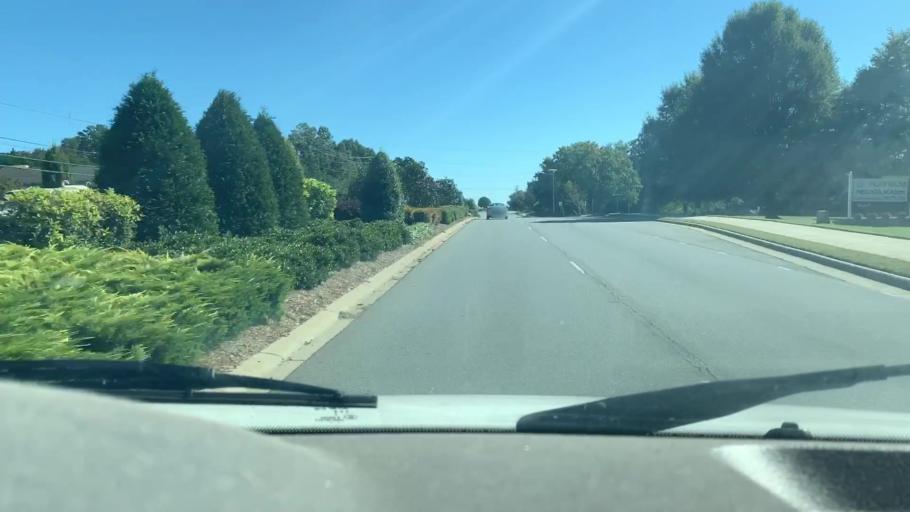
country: US
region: North Carolina
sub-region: Mecklenburg County
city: Huntersville
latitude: 35.4416
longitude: -80.8578
